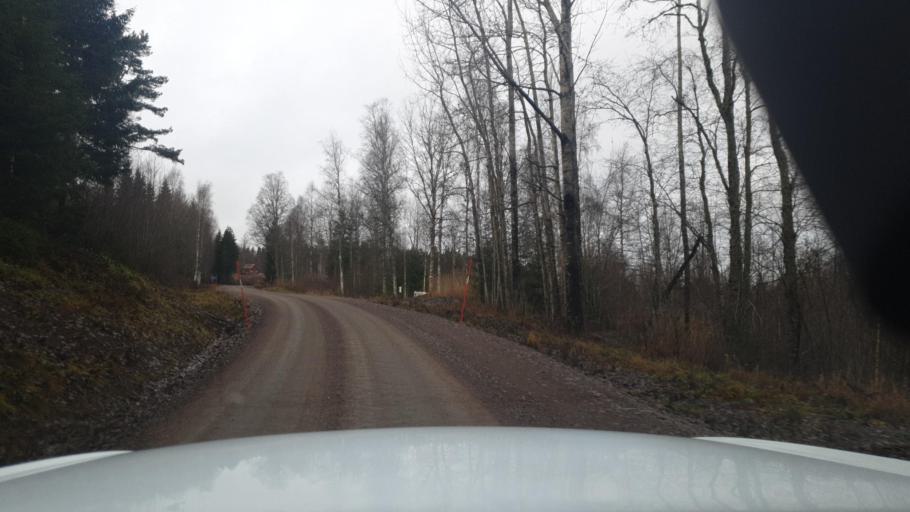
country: SE
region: Vaermland
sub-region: Eda Kommun
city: Charlottenberg
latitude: 60.0915
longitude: 12.4991
